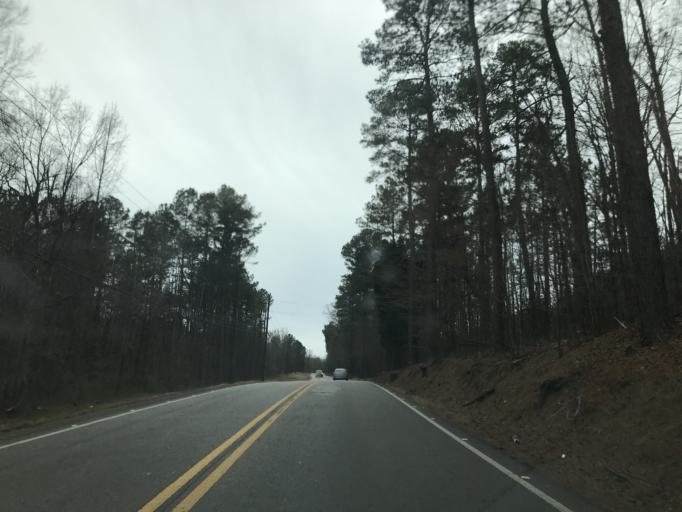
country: US
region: Alabama
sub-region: Shelby County
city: Brook Highland
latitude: 33.4638
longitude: -86.6416
